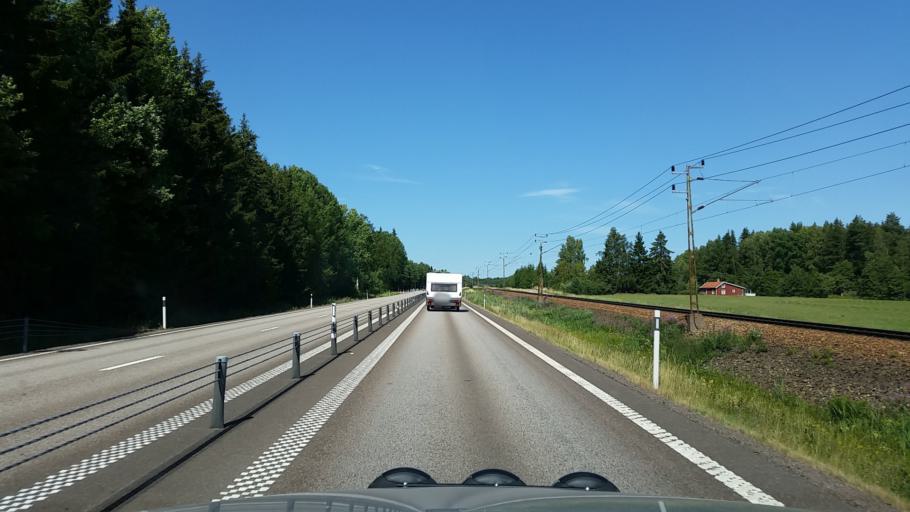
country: SE
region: Vaestra Goetaland
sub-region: Melleruds Kommun
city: Mellerud
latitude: 58.8602
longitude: 12.5588
